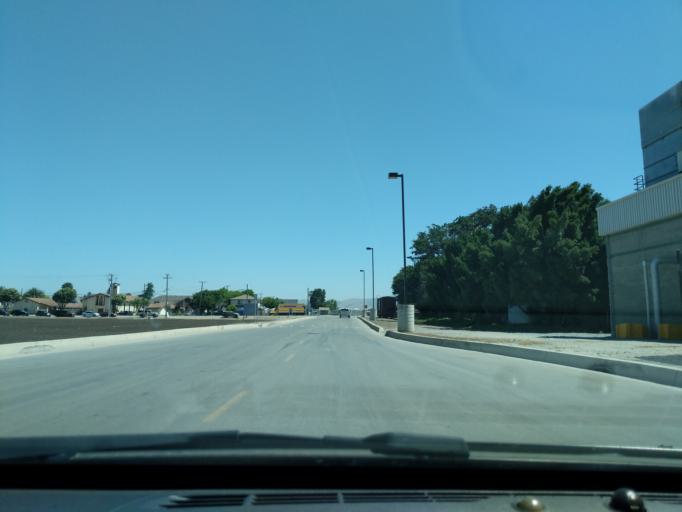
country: US
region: California
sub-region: Monterey County
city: Salinas
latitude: 36.6202
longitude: -121.6457
